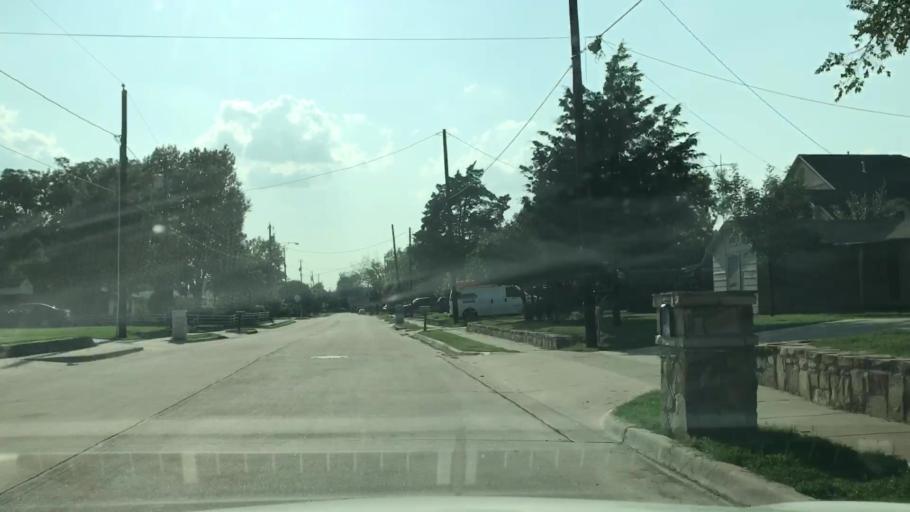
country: US
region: Texas
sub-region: Dallas County
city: Irving
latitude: 32.8199
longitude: -96.9390
